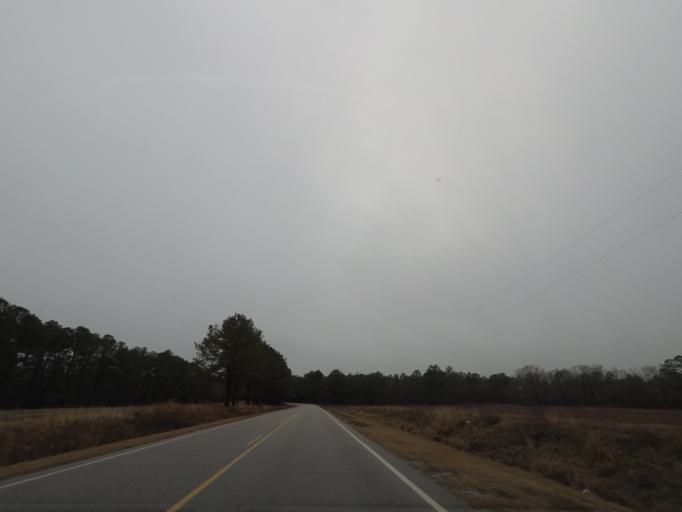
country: US
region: North Carolina
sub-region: Cumberland County
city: Spring Lake
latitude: 35.2691
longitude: -78.9942
